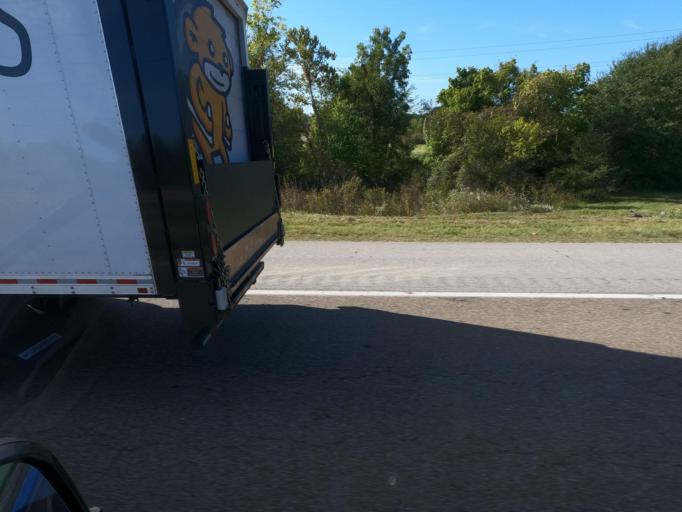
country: US
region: Tennessee
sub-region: Shelby County
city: Millington
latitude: 35.3290
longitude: -89.8905
